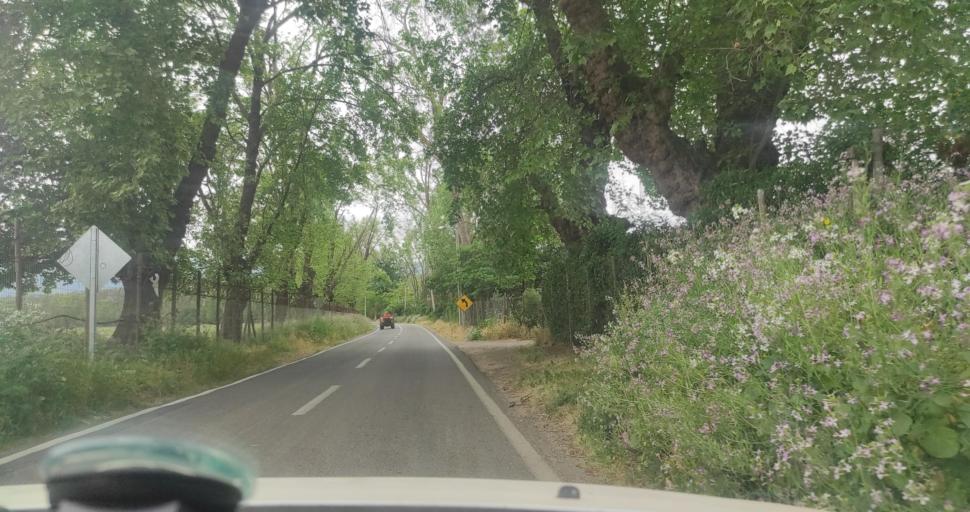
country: CL
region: Valparaiso
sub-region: Provincia de Marga Marga
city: Limache
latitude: -33.0293
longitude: -71.2397
